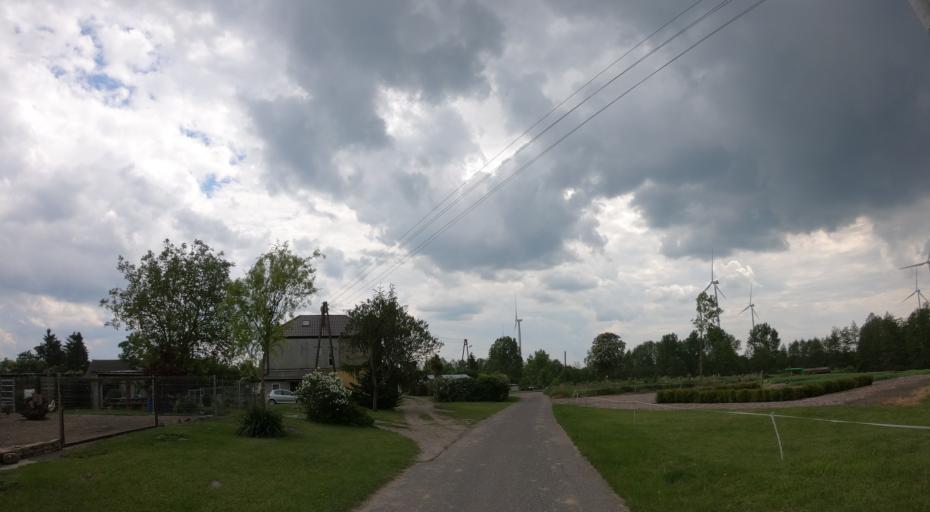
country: PL
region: West Pomeranian Voivodeship
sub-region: Powiat pyrzycki
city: Kozielice
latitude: 53.1492
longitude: 14.7913
